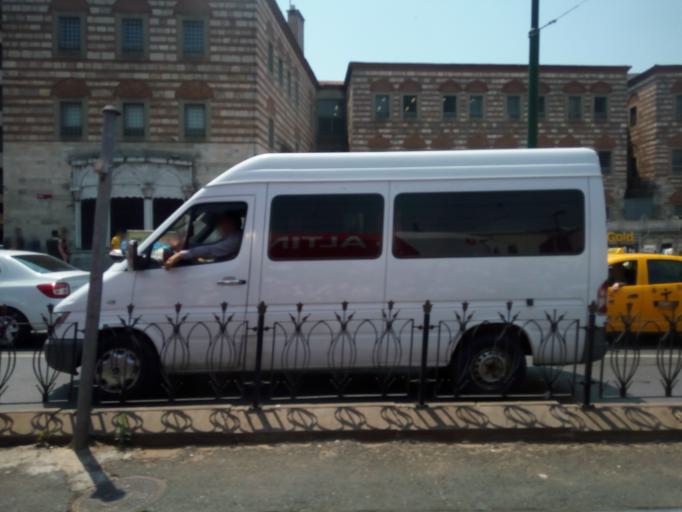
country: TR
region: Istanbul
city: Istanbul
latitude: 41.0092
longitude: 28.9630
